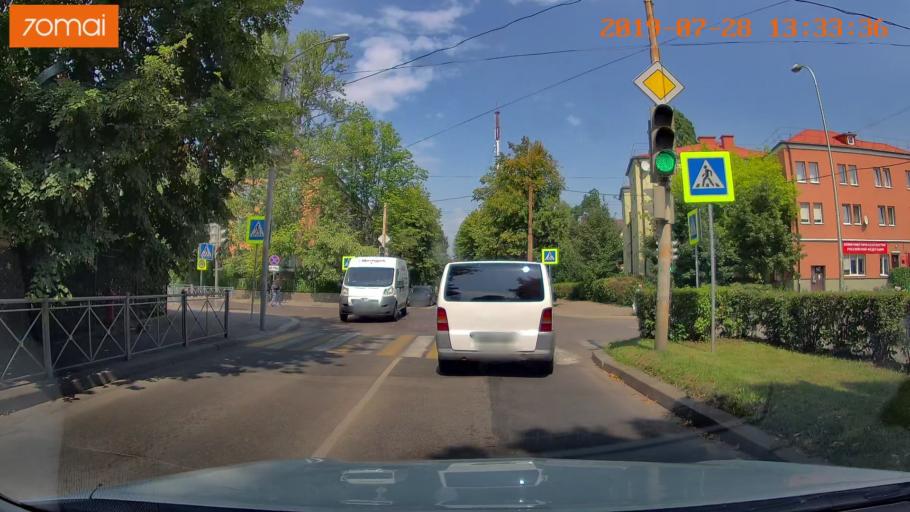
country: RU
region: Kaliningrad
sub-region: Gorod Kaliningrad
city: Kaliningrad
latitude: 54.7245
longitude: 20.4939
